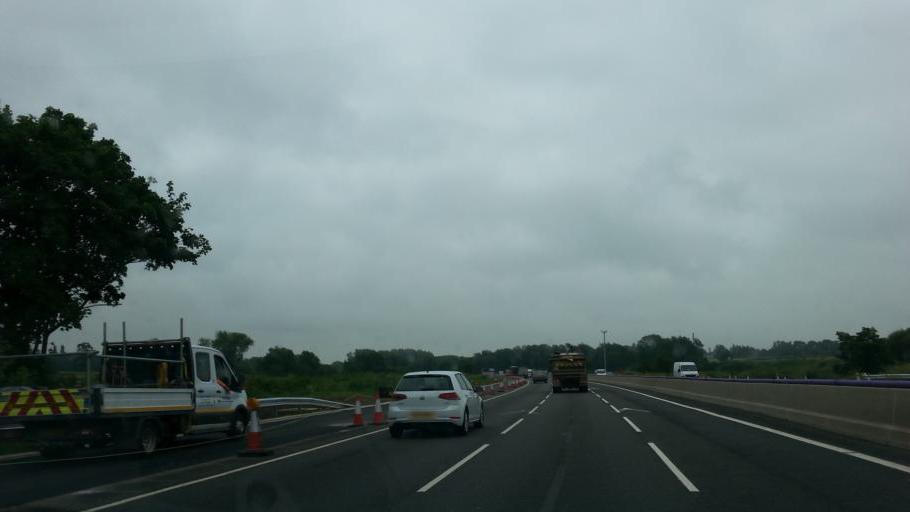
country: GB
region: England
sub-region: Northamptonshire
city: Long Buckby
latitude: 52.2695
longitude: -1.0923
